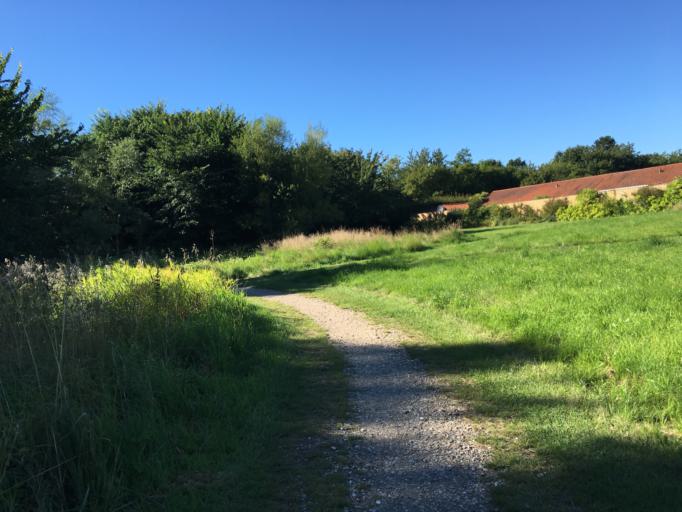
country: DK
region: Capital Region
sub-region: Fredensborg Kommune
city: Niva
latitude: 55.9286
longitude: 12.5038
